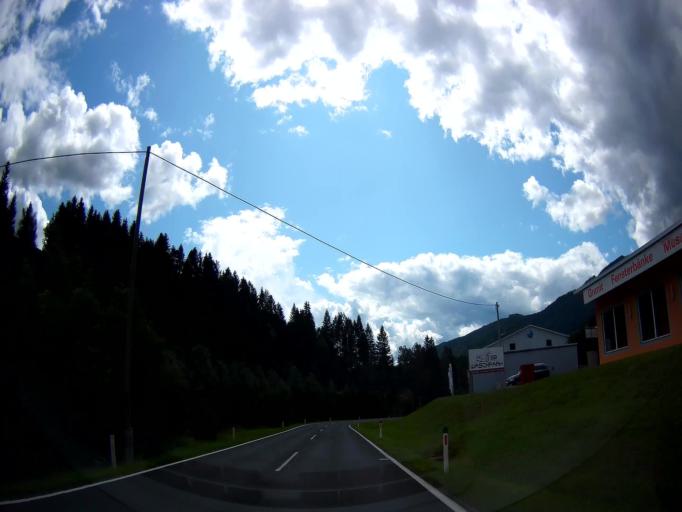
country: AT
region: Carinthia
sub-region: Politischer Bezirk Spittal an der Drau
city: Trebesing
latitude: 46.8917
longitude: 13.5240
